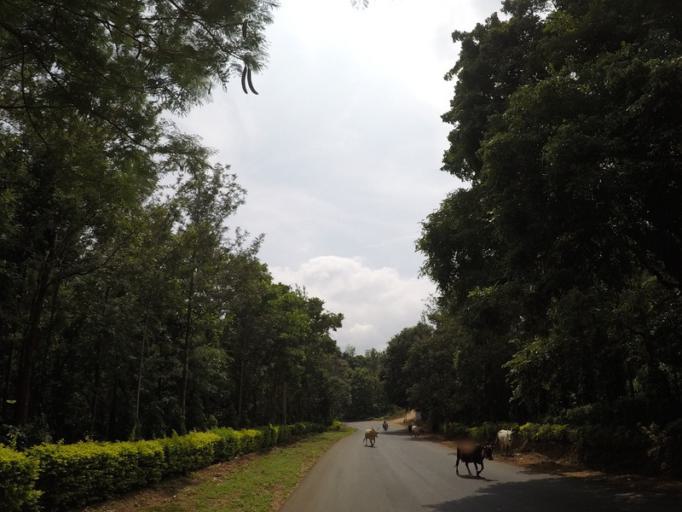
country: IN
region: Karnataka
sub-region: Chikmagalur
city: Chikmagalur
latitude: 13.4099
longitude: 75.7964
